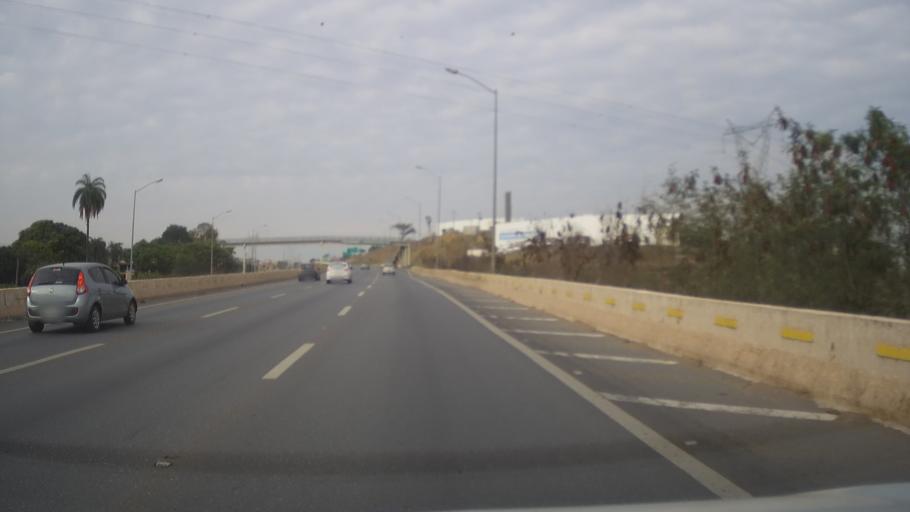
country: BR
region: Minas Gerais
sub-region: Vespasiano
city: Vespasiano
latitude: -19.7322
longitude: -43.9433
